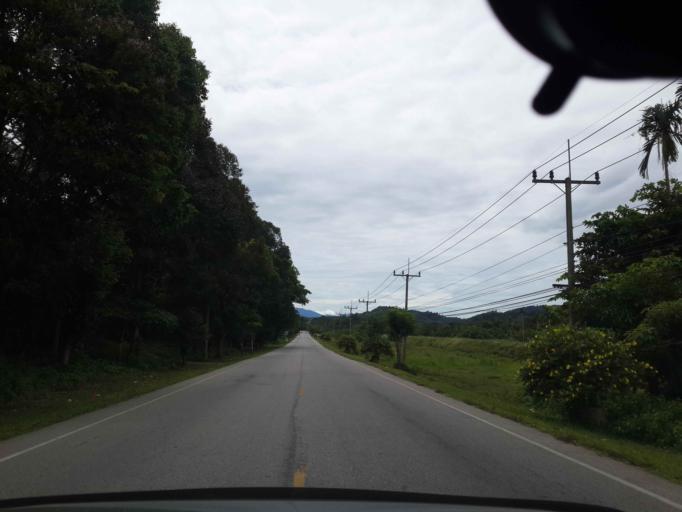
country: TH
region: Narathiwat
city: Yi-ngo
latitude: 6.3504
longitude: 101.6201
